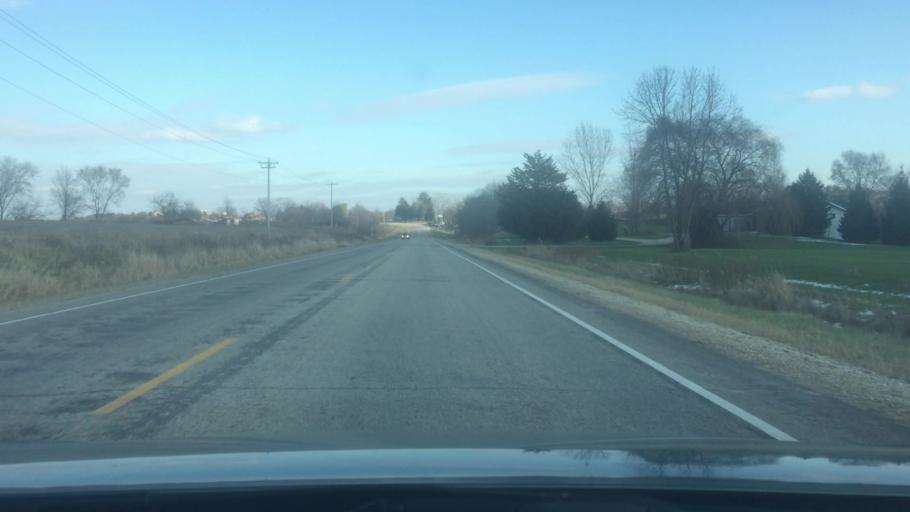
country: US
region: Wisconsin
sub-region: Walworth County
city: Whitewater
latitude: 42.9310
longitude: -88.6871
